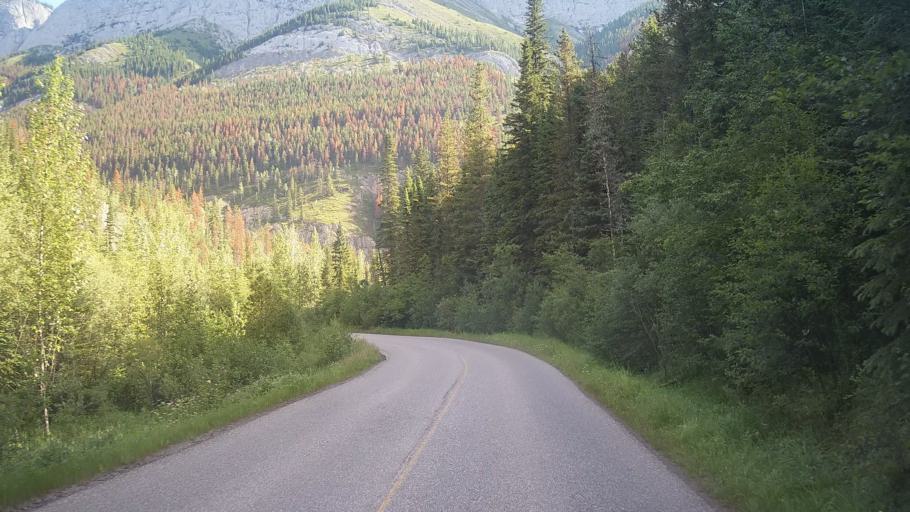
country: CA
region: Alberta
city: Hinton
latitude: 53.1765
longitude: -117.8386
